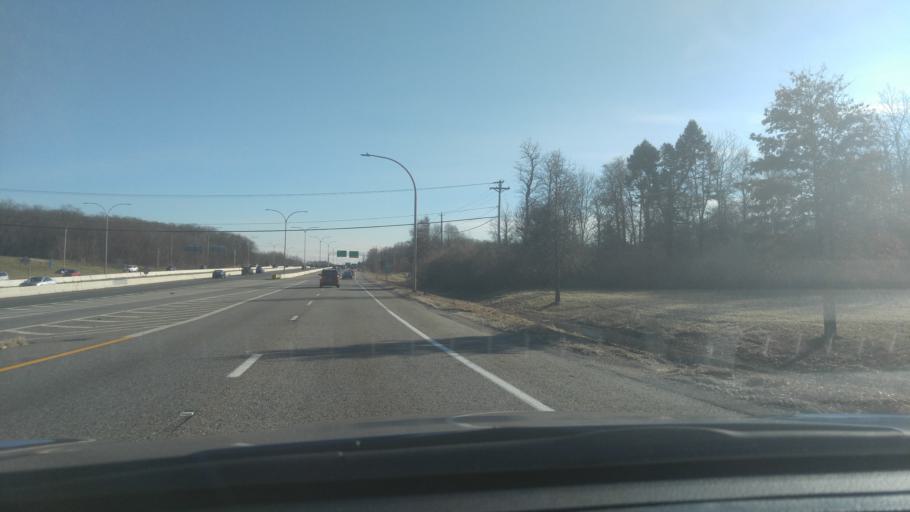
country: US
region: Rhode Island
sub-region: Providence County
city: Cumberland Hill
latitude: 41.9487
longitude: -71.4835
